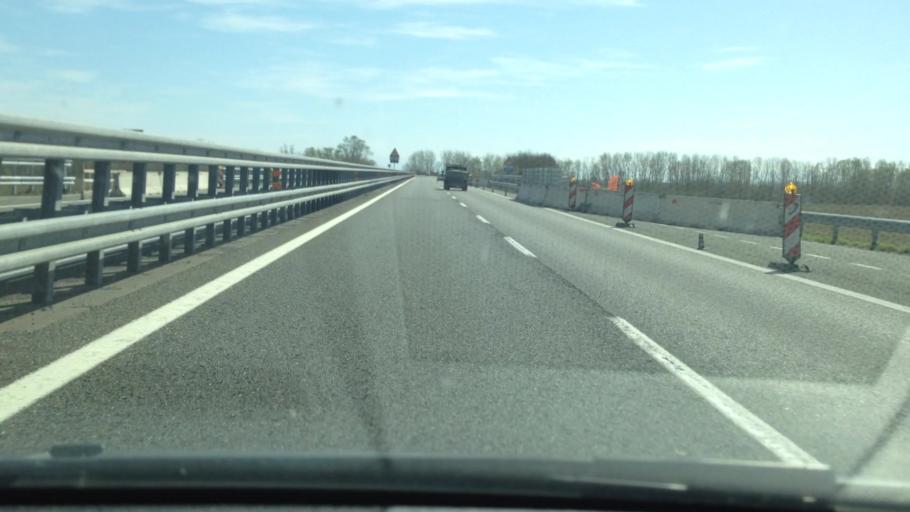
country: IT
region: Piedmont
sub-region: Provincia di Alessandria
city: Pietra Marazzi
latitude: 44.9343
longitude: 8.6574
